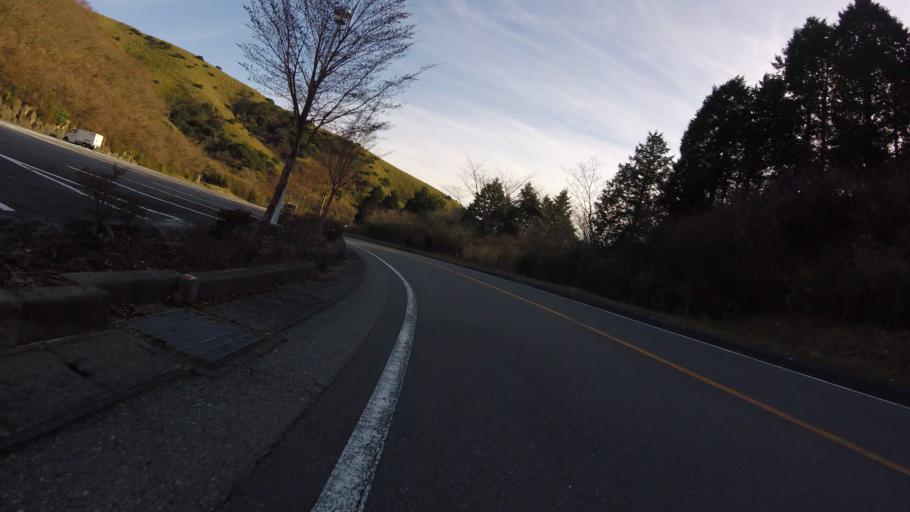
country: JP
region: Kanagawa
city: Yugawara
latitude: 35.1263
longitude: 139.0371
